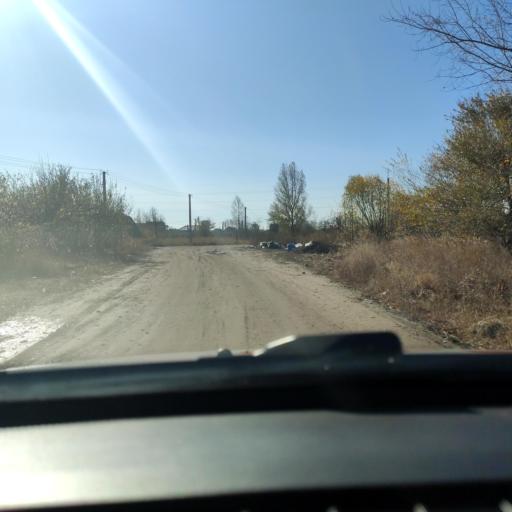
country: RU
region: Voronezj
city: Shilovo
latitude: 51.5200
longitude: 39.1539
